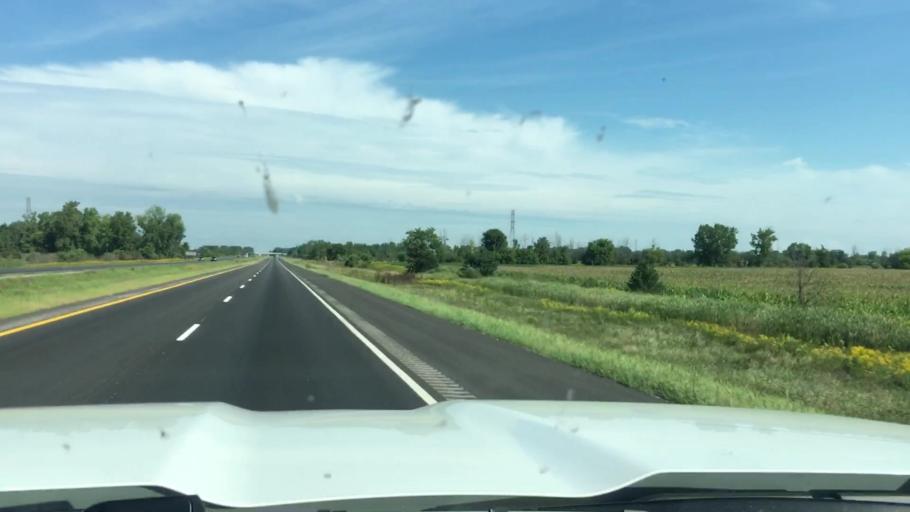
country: US
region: Michigan
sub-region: Saginaw County
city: Freeland
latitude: 43.5504
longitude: -84.1387
